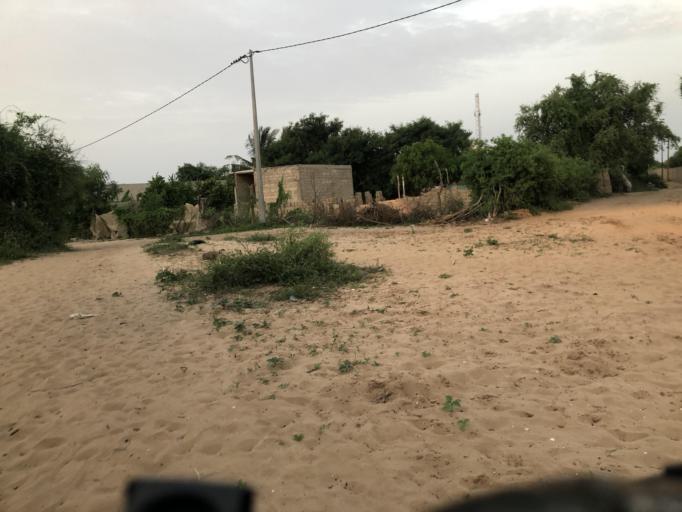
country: SN
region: Saint-Louis
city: Saint-Louis
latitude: 16.0645
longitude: -16.4318
